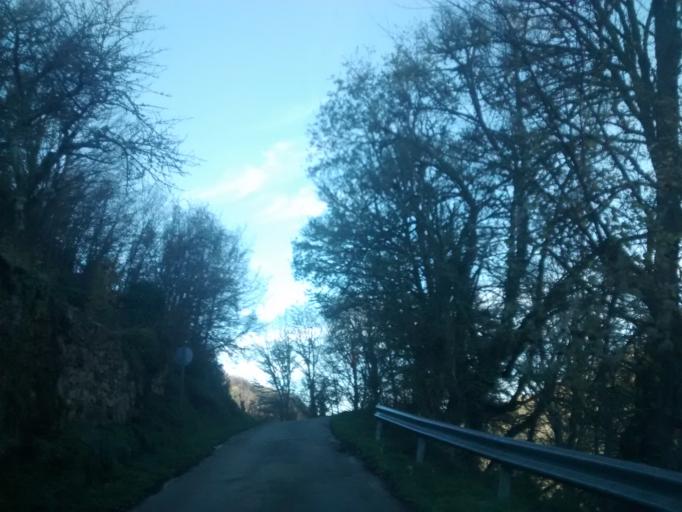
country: ES
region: Cantabria
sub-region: Provincia de Cantabria
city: San Pedro del Romeral
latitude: 42.9689
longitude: -3.7447
